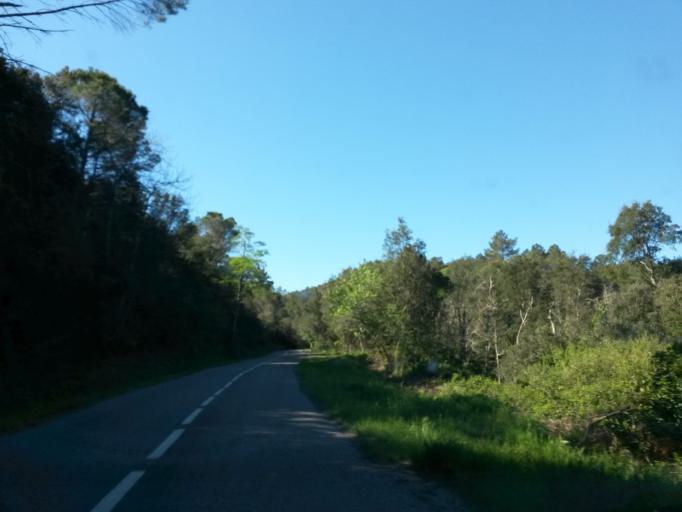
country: ES
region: Catalonia
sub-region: Provincia de Girona
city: Madremanya
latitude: 41.9848
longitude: 2.9482
